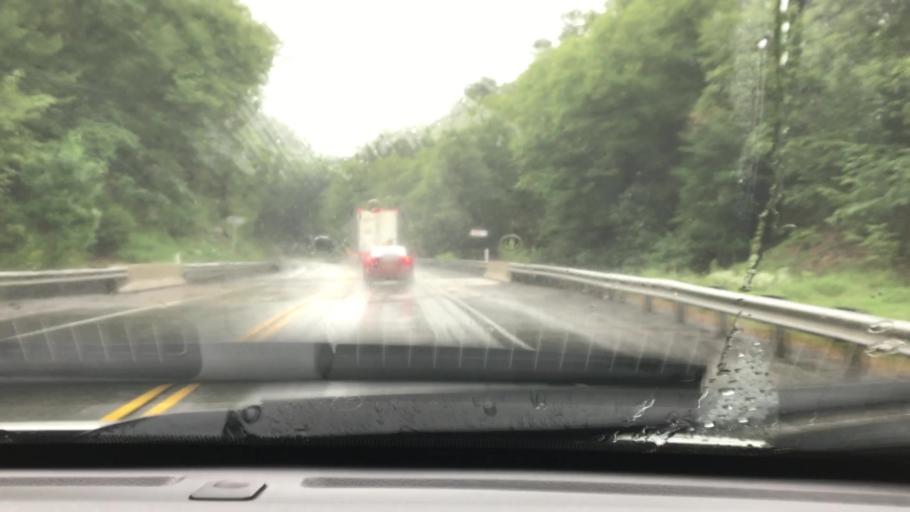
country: US
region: Pennsylvania
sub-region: Clearfield County
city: Osceola Mills
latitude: 40.7665
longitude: -78.2352
